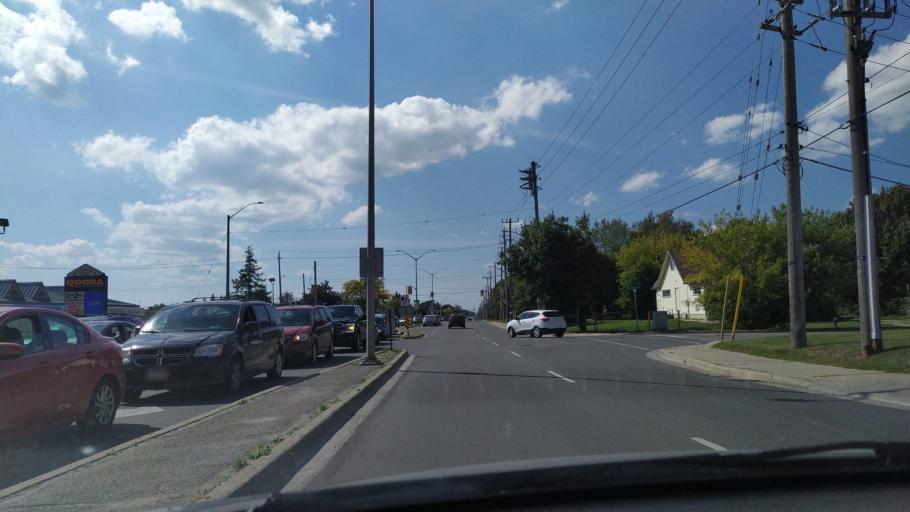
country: CA
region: Ontario
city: London
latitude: 42.9435
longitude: -81.2264
